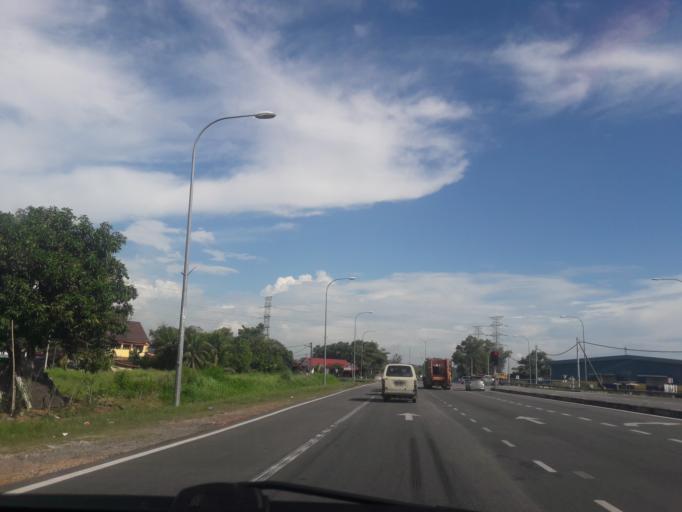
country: MY
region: Kedah
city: Sungai Petani
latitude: 5.6185
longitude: 100.4661
